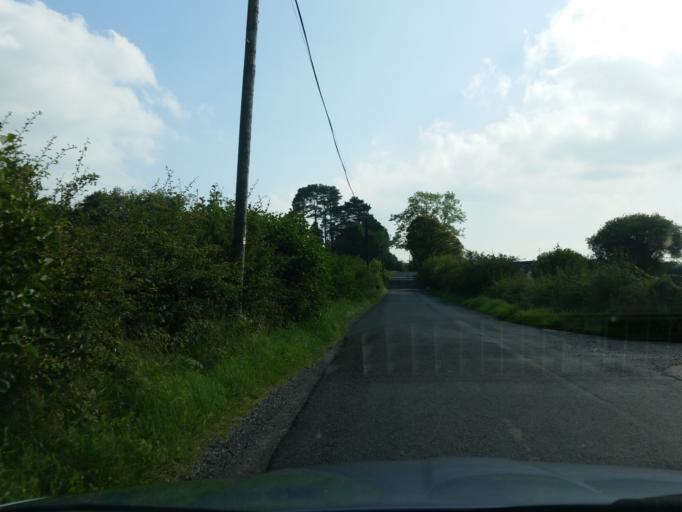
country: GB
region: Northern Ireland
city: Ballinamallard
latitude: 54.3500
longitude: -7.5496
